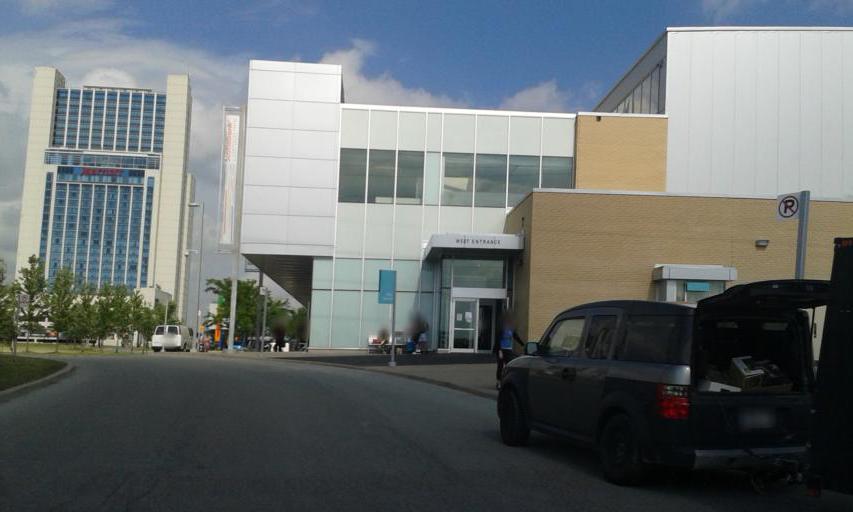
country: CA
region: Ontario
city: Niagara Falls
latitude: 43.0764
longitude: -79.0866
